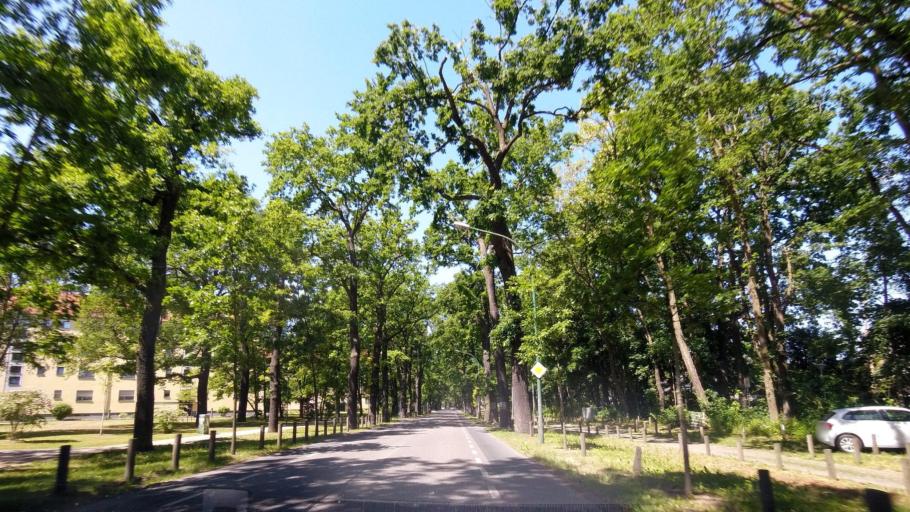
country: DE
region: Brandenburg
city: Potsdam
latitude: 52.3701
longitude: 13.0955
